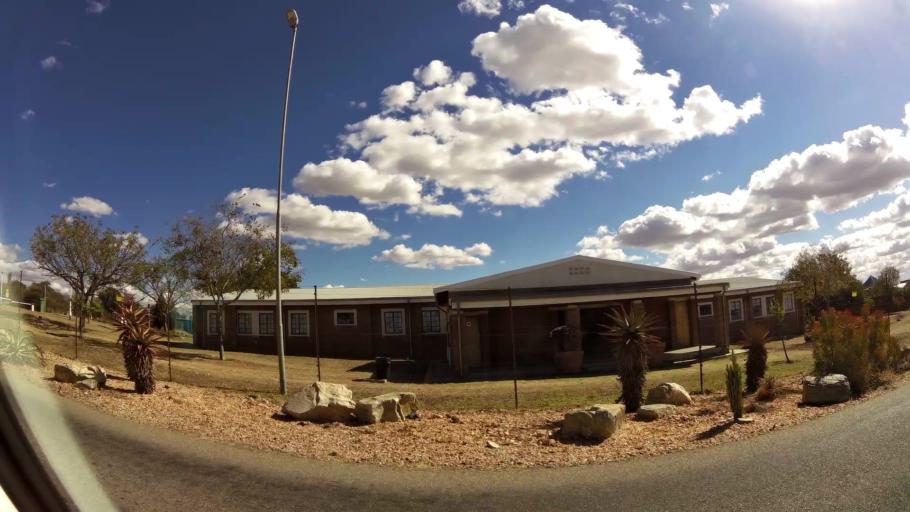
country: ZA
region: Limpopo
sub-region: Capricorn District Municipality
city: Polokwane
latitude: -23.8685
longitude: 29.5095
